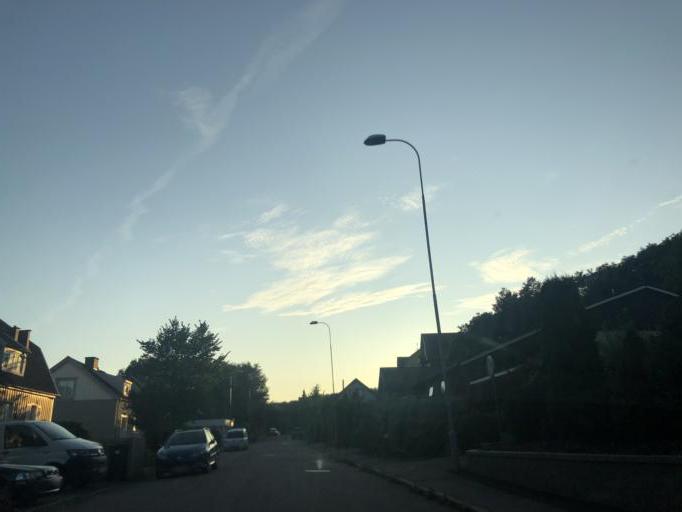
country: SE
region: Vaestra Goetaland
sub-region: Goteborg
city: Goeteborg
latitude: 57.7320
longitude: 11.9799
